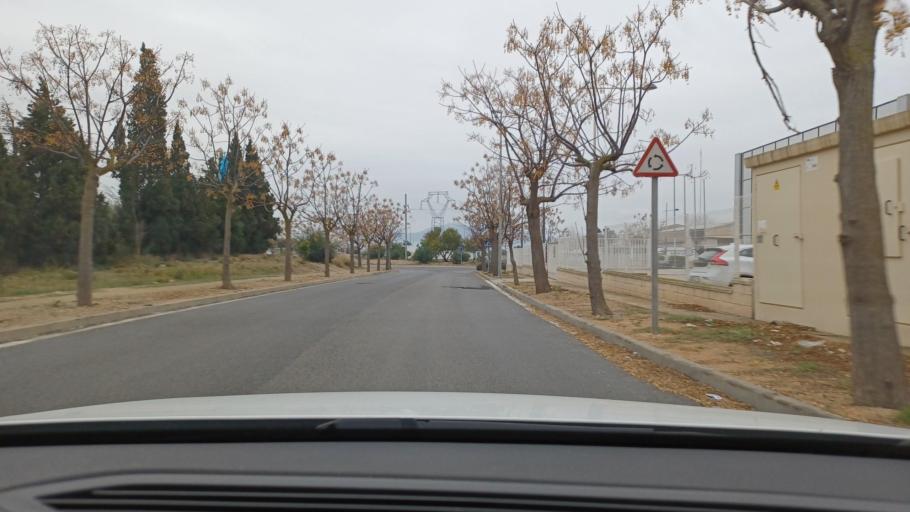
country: ES
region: Catalonia
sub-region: Provincia de Tarragona
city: Amposta
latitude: 40.7563
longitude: 0.6004
